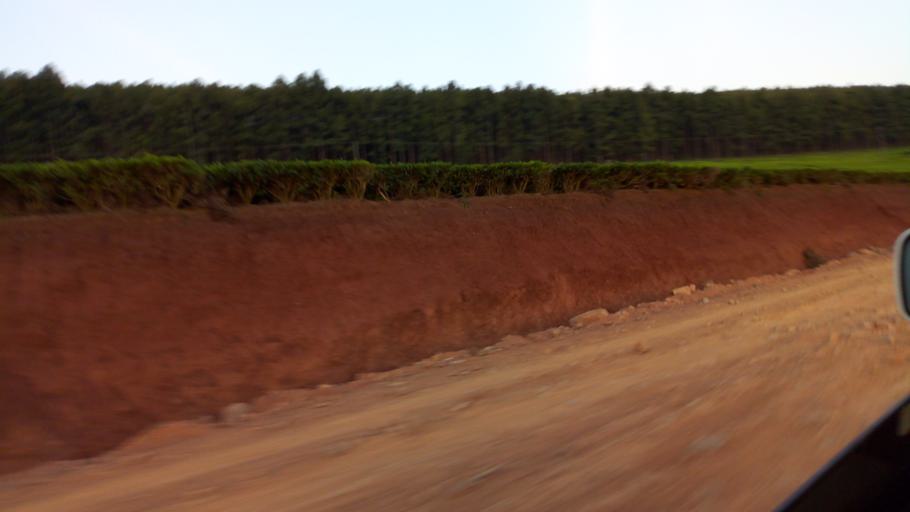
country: KE
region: Kericho
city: Sotik
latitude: -0.6021
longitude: 35.0611
